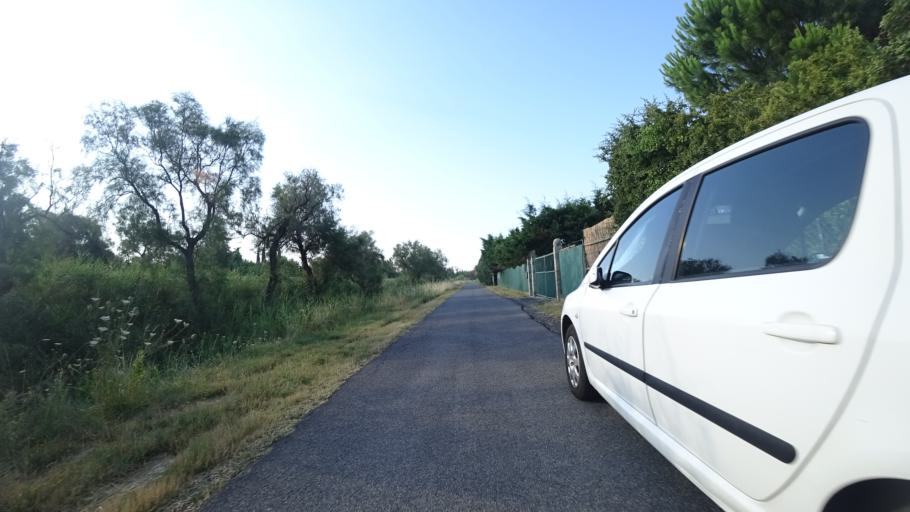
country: FR
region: Languedoc-Roussillon
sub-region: Departement des Pyrenees-Orientales
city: Sainte-Marie-Plage
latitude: 42.7281
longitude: 3.0284
